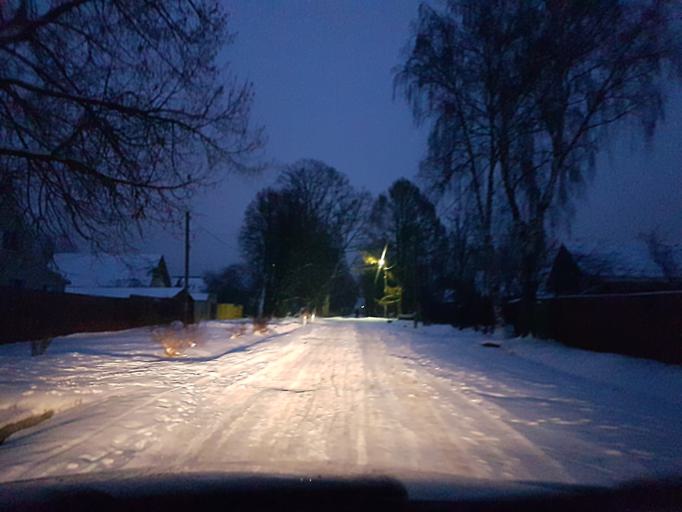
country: RU
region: Tverskaya
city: Novozavidovskiy
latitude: 56.5559
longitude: 36.4230
